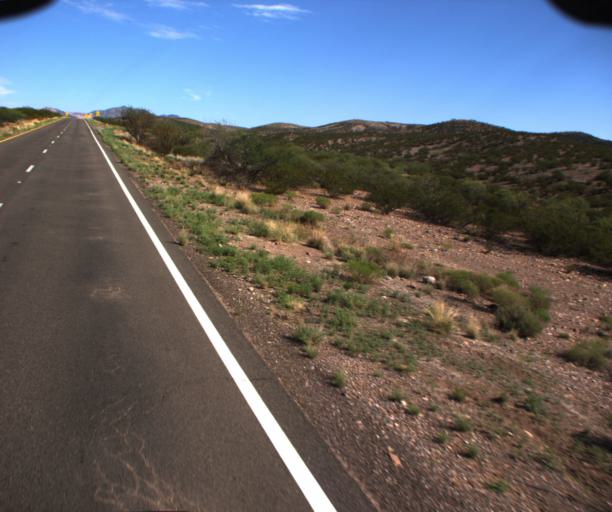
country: US
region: Arizona
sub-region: Greenlee County
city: Clifton
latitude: 32.9986
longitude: -109.2755
